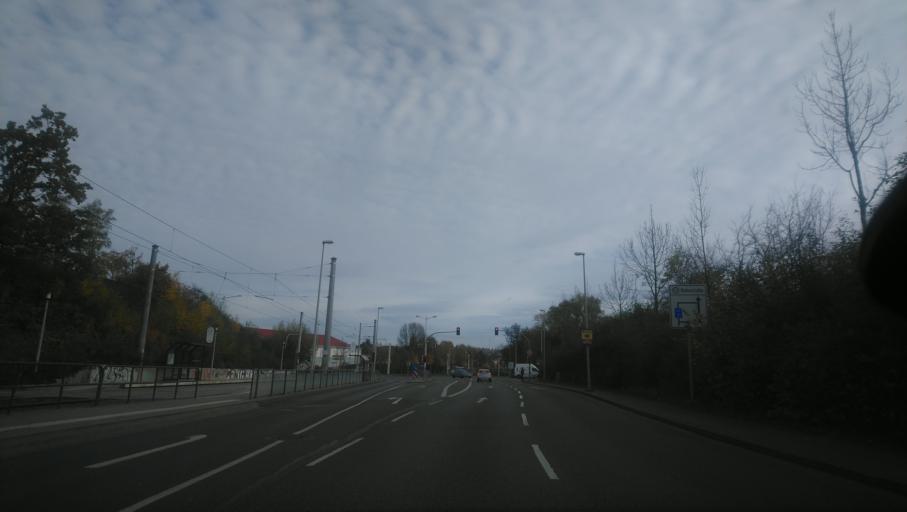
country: DE
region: Saxony
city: Zwickau
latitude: 50.7000
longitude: 12.4843
